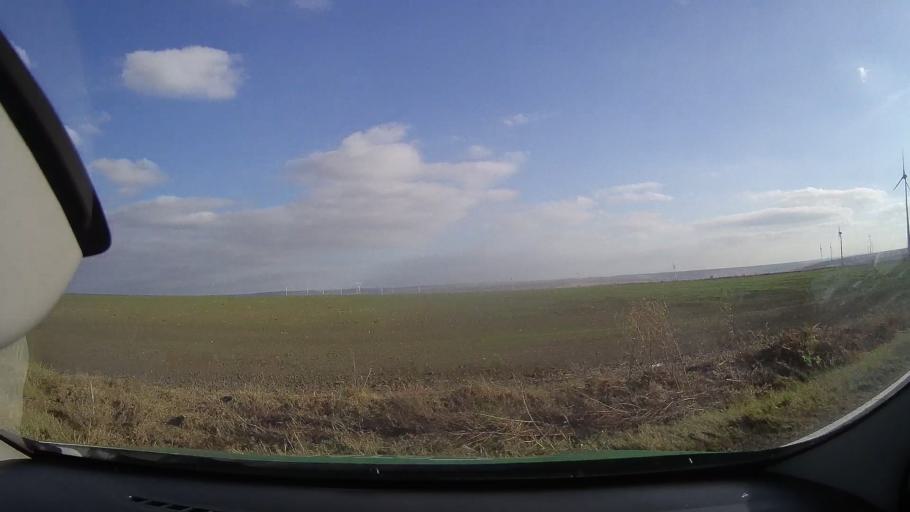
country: RO
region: Tulcea
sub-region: Comuna Topolog
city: Topolog
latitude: 44.8125
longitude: 28.2549
